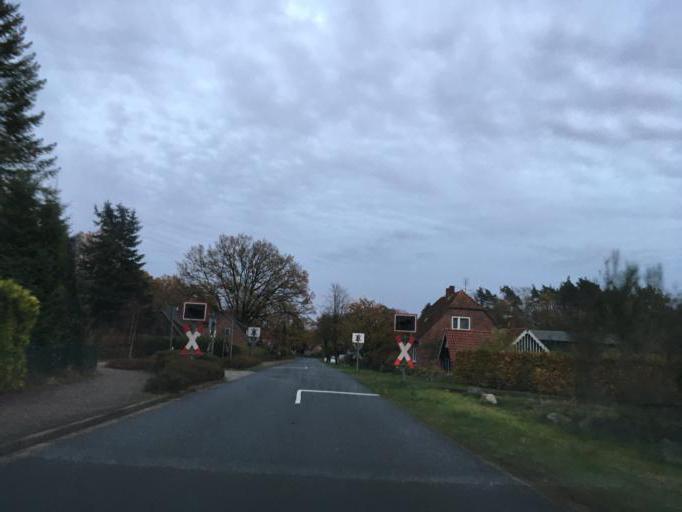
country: DE
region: Lower Saxony
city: Bispingen
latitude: 53.0970
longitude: 10.0180
